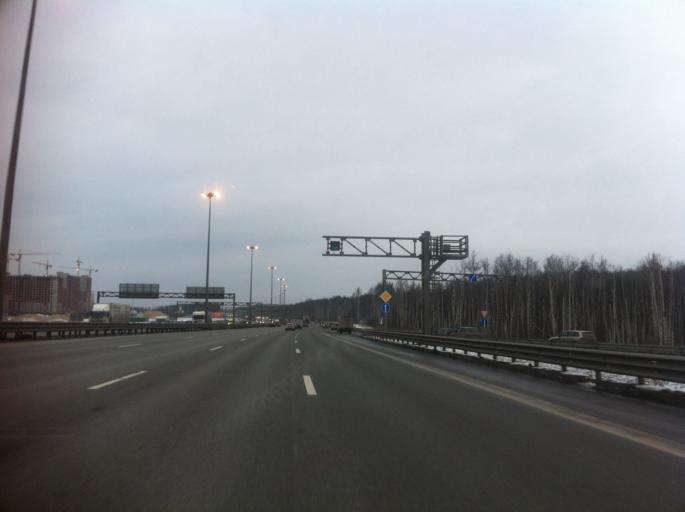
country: RU
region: Leningrad
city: Rybatskoye
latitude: 59.8877
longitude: 30.5249
